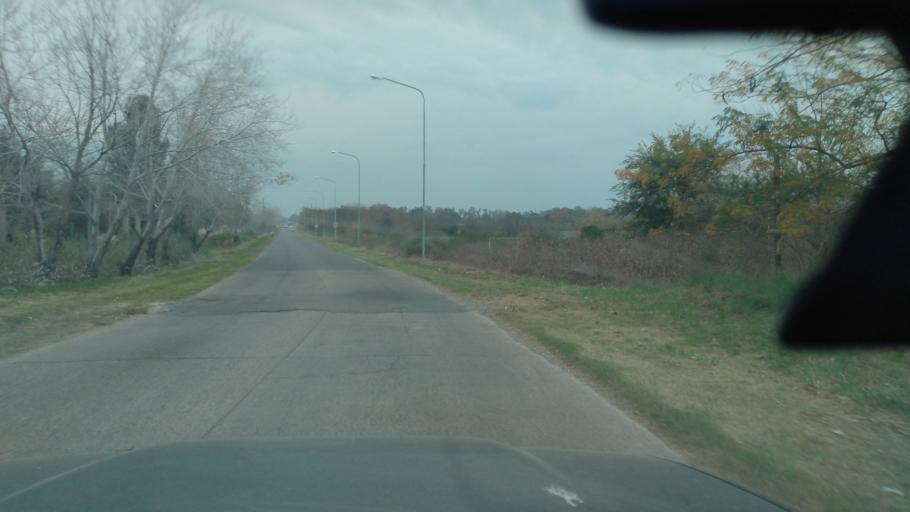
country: AR
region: Buenos Aires
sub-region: Partido de Lujan
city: Lujan
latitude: -34.5663
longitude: -59.1455
